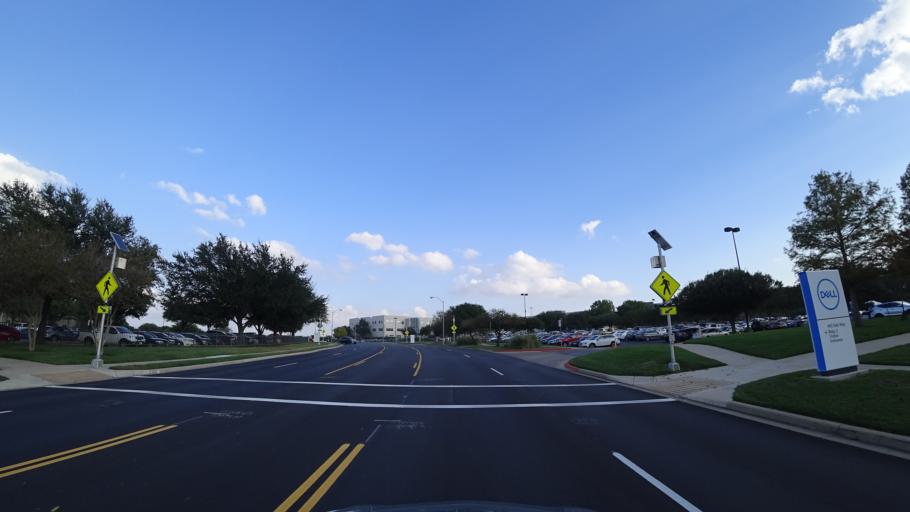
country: US
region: Texas
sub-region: Williamson County
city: Round Rock
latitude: 30.4856
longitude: -97.6653
